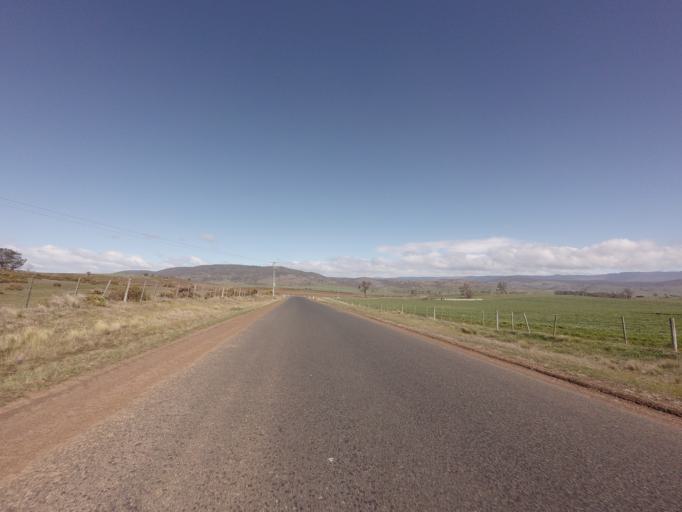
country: AU
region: Tasmania
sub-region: Northern Midlands
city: Evandale
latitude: -41.8975
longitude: 147.4068
